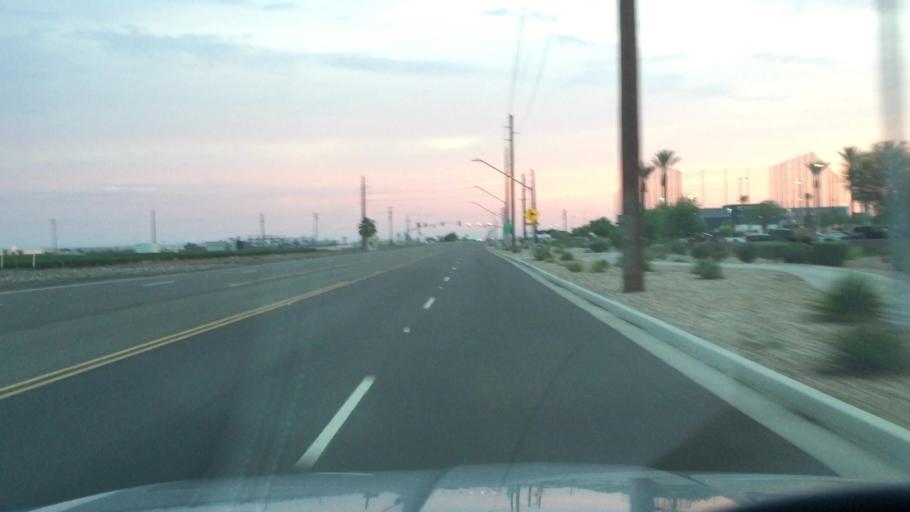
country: US
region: Arizona
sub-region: Maricopa County
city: Peoria
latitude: 33.5197
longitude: -112.2723
